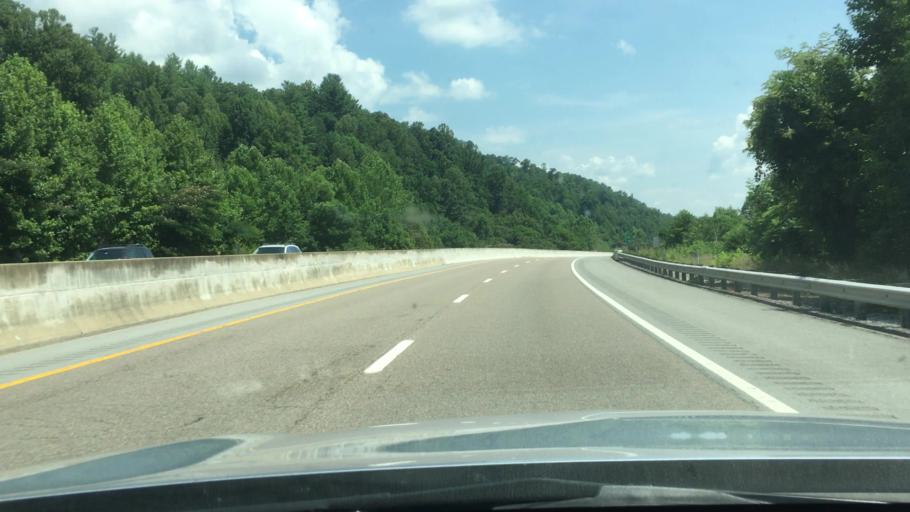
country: US
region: Tennessee
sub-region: Unicoi County
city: Banner Hill
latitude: 36.0920
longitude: -82.4845
